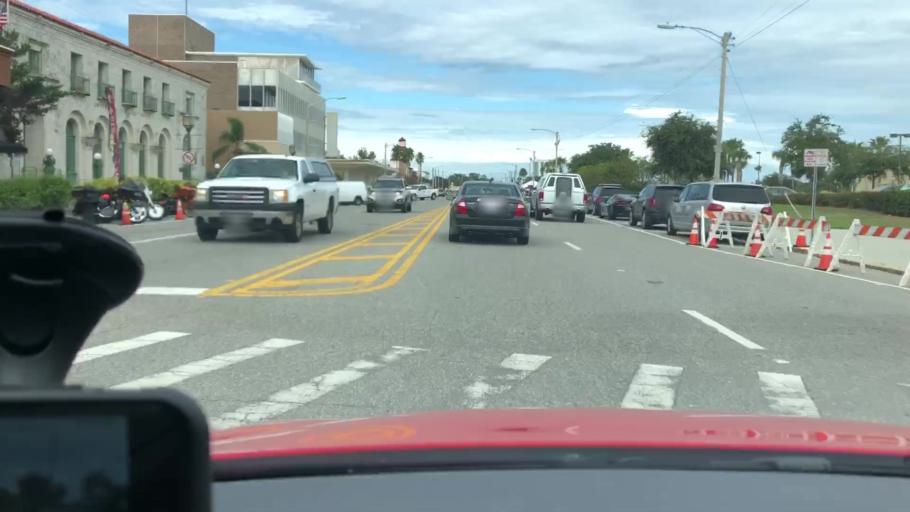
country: US
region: Florida
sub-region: Volusia County
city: Daytona Beach
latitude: 29.2143
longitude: -81.0203
